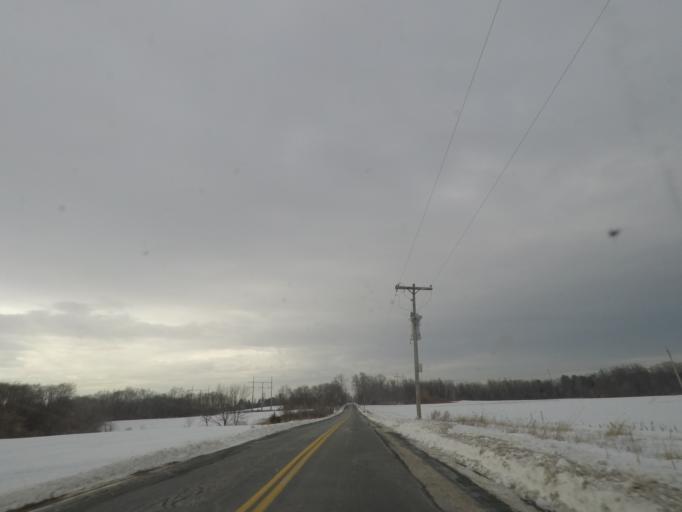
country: US
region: New York
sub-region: Rensselaer County
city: Castleton-on-Hudson
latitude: 42.4931
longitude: -73.7395
